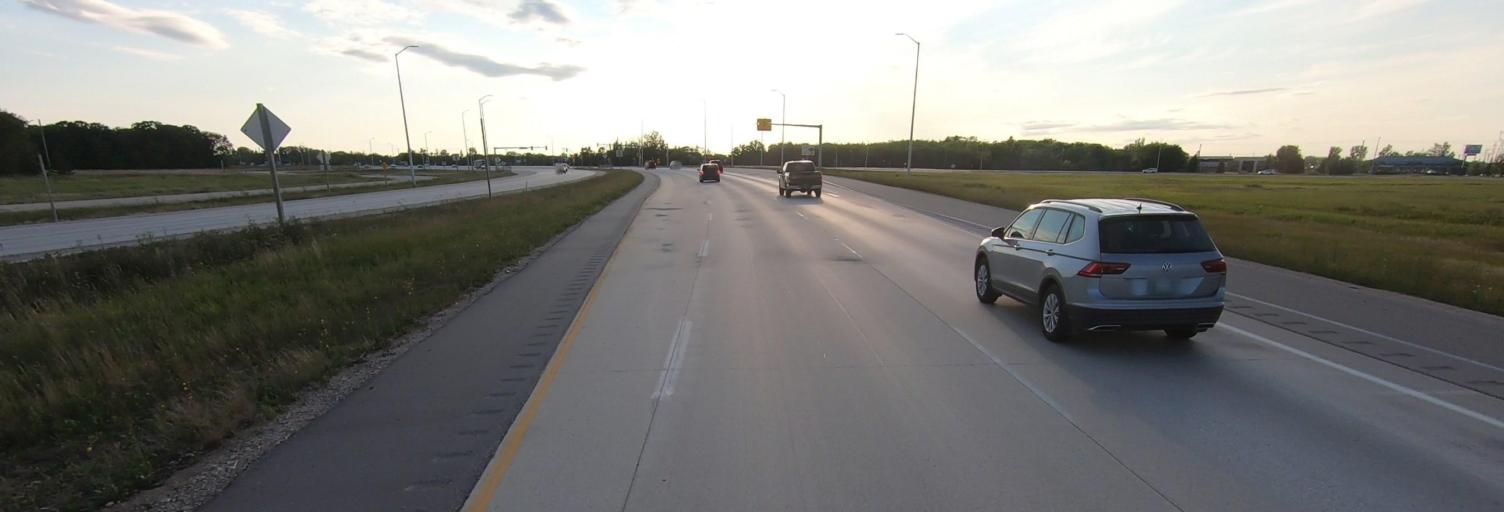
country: CA
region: Manitoba
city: Winnipeg
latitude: 49.9671
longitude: -97.0094
